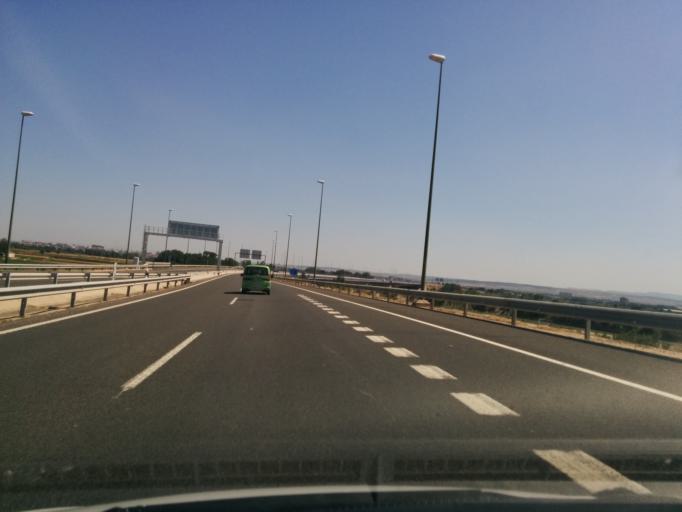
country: ES
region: Aragon
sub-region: Provincia de Zaragoza
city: Zaragoza
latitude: 41.6278
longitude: -0.8435
